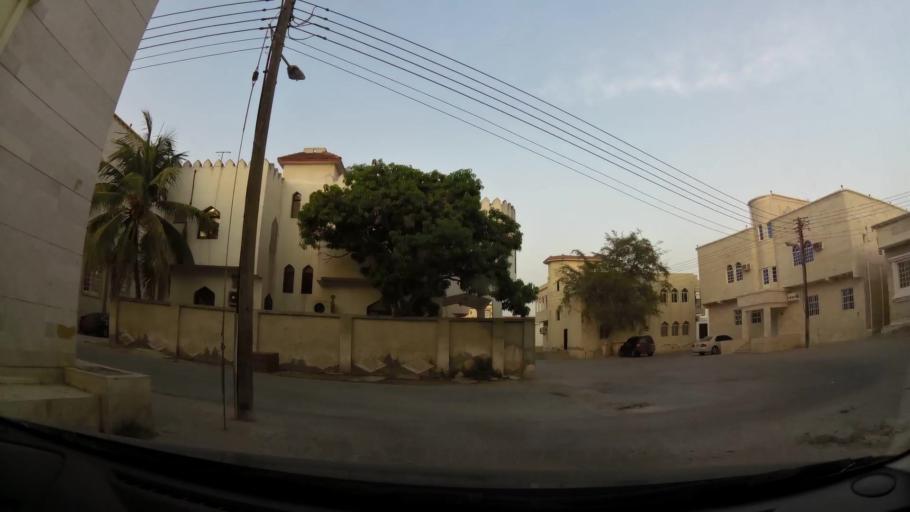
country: OM
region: Zufar
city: Salalah
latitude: 17.0207
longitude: 54.1258
